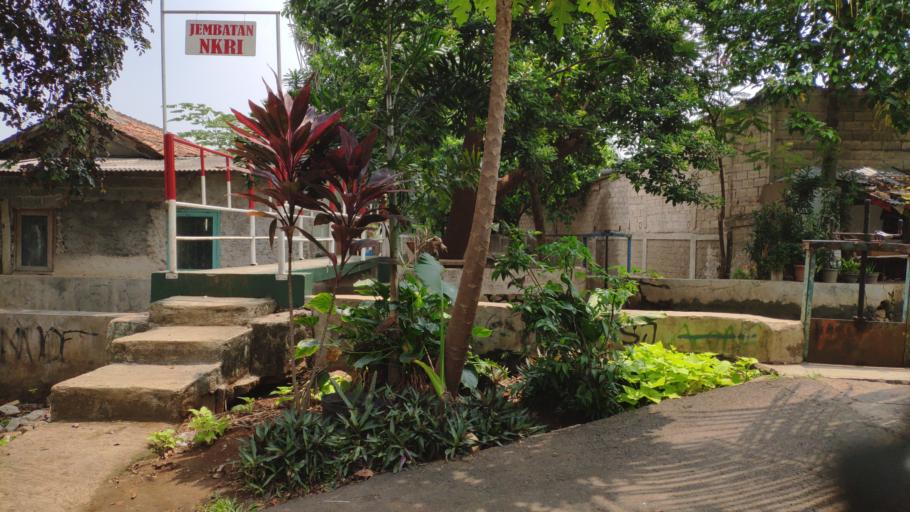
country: ID
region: West Java
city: Depok
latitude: -6.3179
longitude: 106.8352
